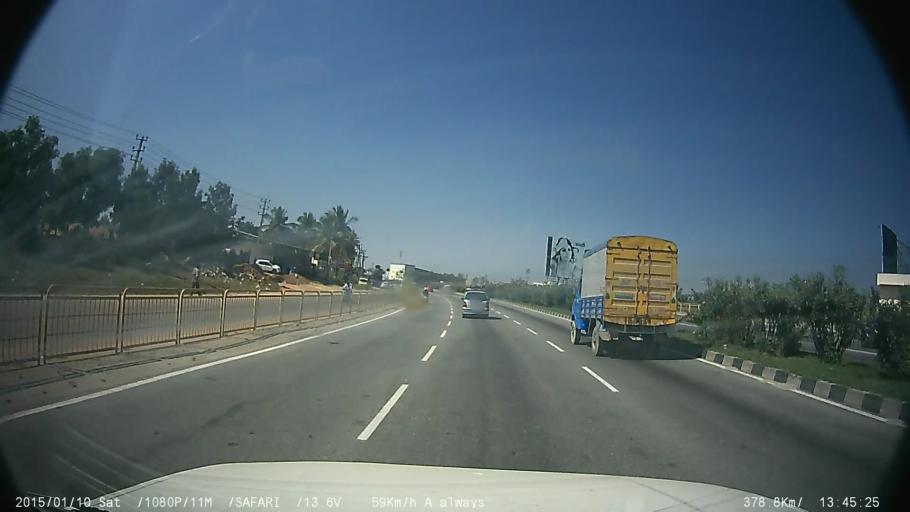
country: IN
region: Karnataka
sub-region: Bangalore Urban
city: Anekal
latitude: 12.7972
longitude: 77.7177
